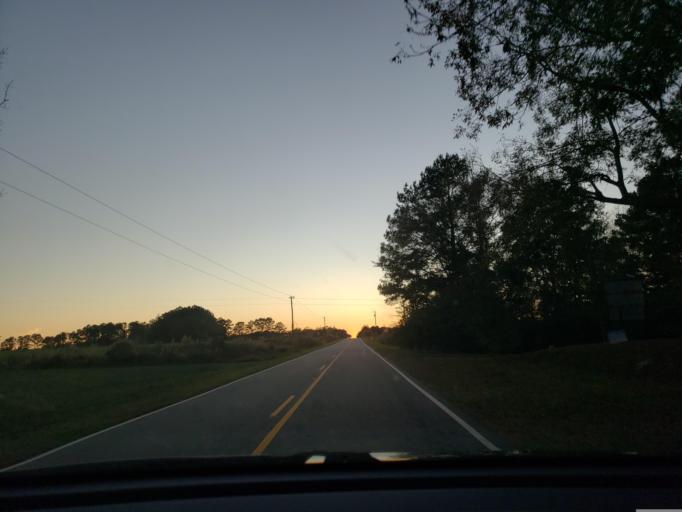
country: US
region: North Carolina
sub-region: Duplin County
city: Beulaville
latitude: 34.7599
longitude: -77.6801
